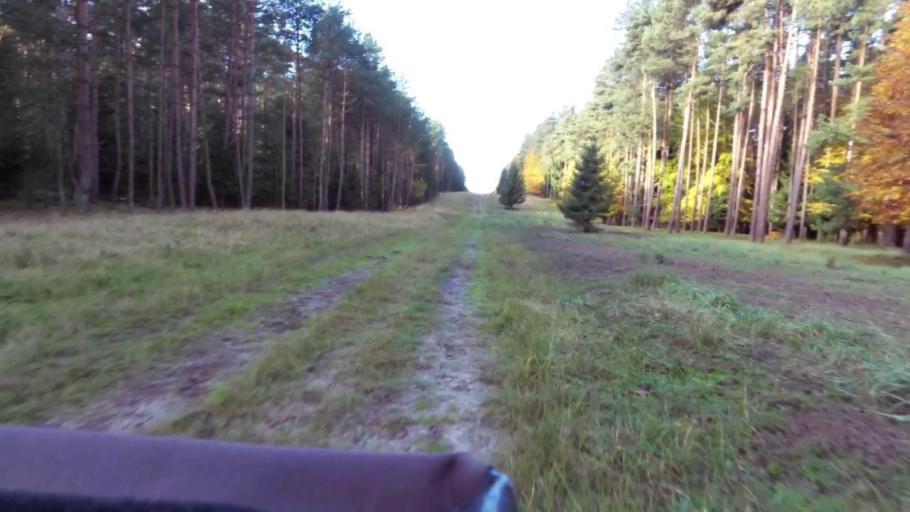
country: PL
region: West Pomeranian Voivodeship
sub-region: Powiat kamienski
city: Miedzyzdroje
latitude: 53.8694
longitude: 14.5006
